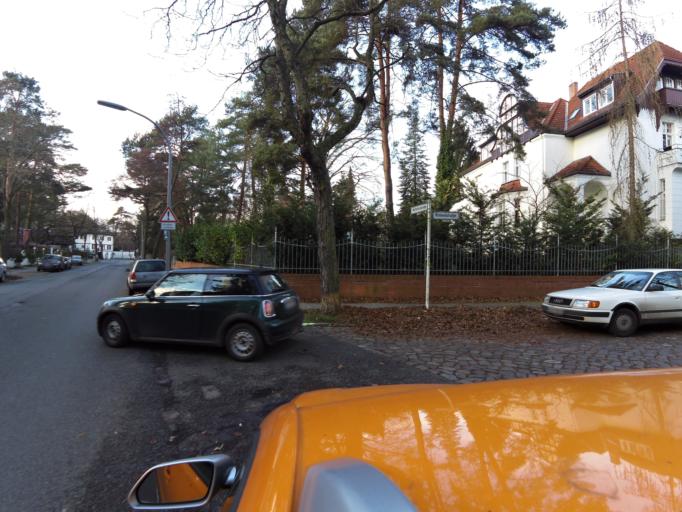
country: DE
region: Berlin
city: Nikolassee
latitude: 52.4347
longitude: 13.2040
